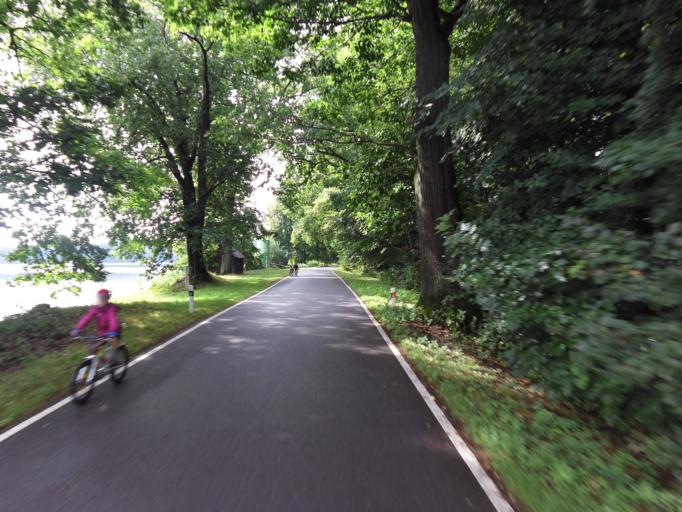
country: CZ
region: Jihocesky
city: Chlum u Trebone
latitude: 48.9454
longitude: 14.9157
